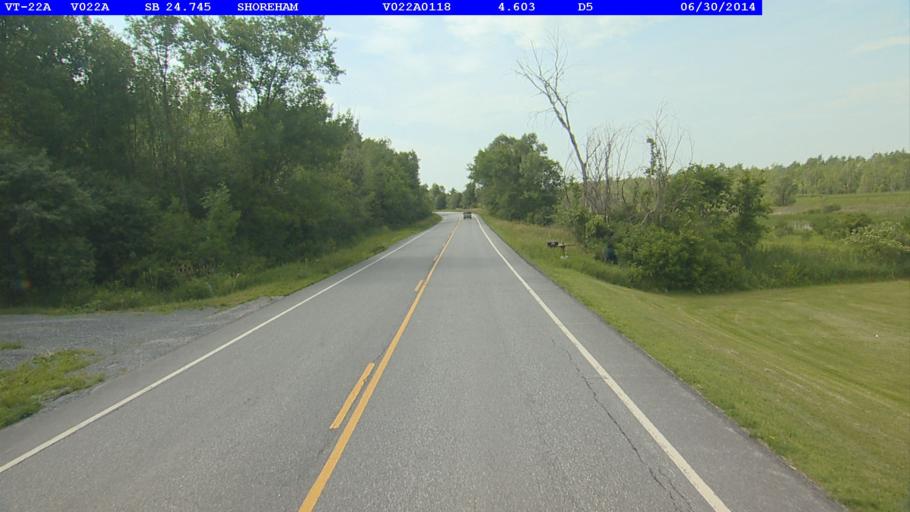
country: US
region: New York
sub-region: Essex County
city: Ticonderoga
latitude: 43.9155
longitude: -73.3122
